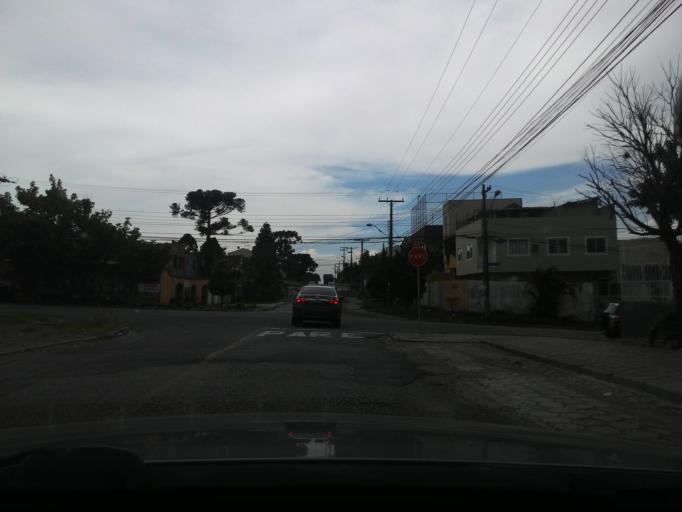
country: BR
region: Parana
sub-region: Pinhais
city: Pinhais
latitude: -25.4466
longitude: -49.2224
